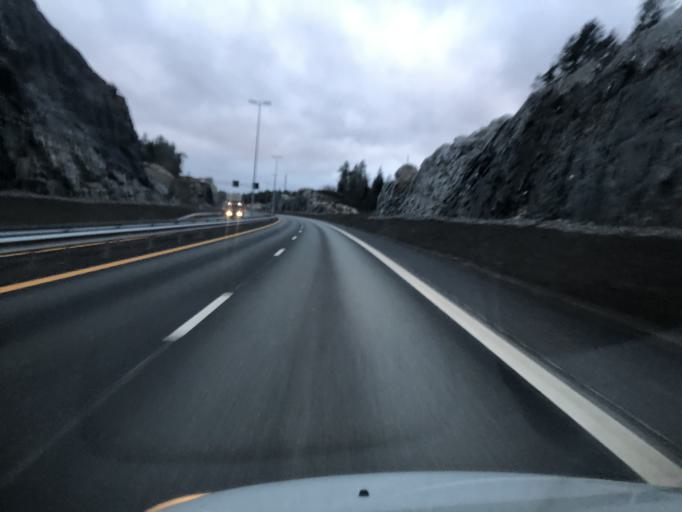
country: NO
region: Aust-Agder
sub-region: Arendal
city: Arendal
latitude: 58.4976
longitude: 8.7776
